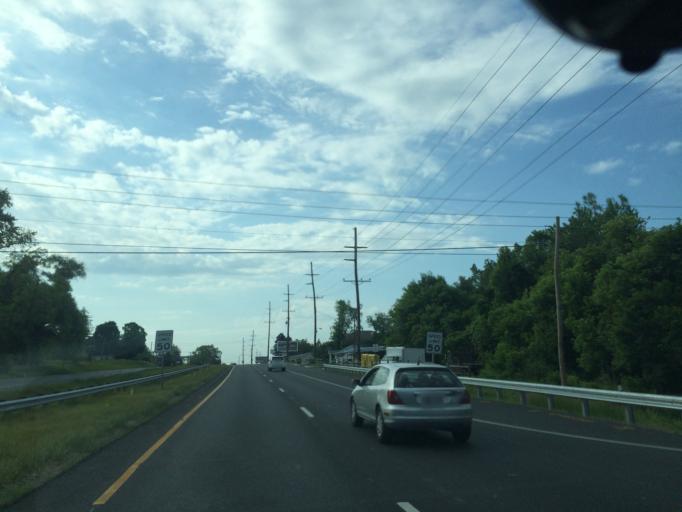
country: US
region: Maryland
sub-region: Baltimore County
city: Reisterstown
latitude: 39.5015
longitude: -76.8975
